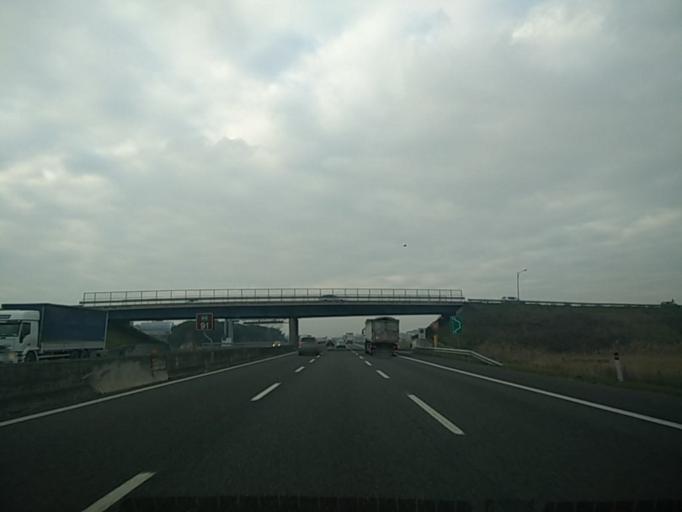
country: IT
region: Emilia-Romagna
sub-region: Forli-Cesena
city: Gatteo-Sant'Angelo
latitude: 44.1234
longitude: 12.3857
